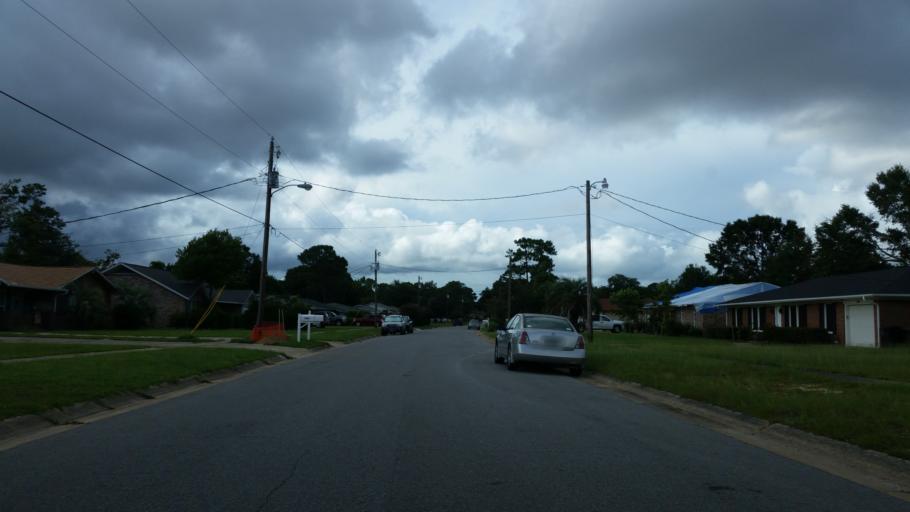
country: US
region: Florida
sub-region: Escambia County
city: Ferry Pass
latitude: 30.5059
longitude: -87.1825
